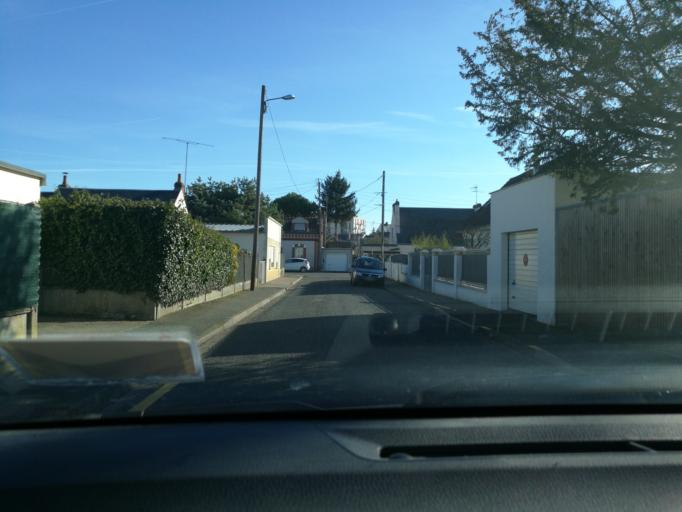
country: FR
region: Centre
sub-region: Departement du Loiret
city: Orleans
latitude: 47.9114
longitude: 1.8905
